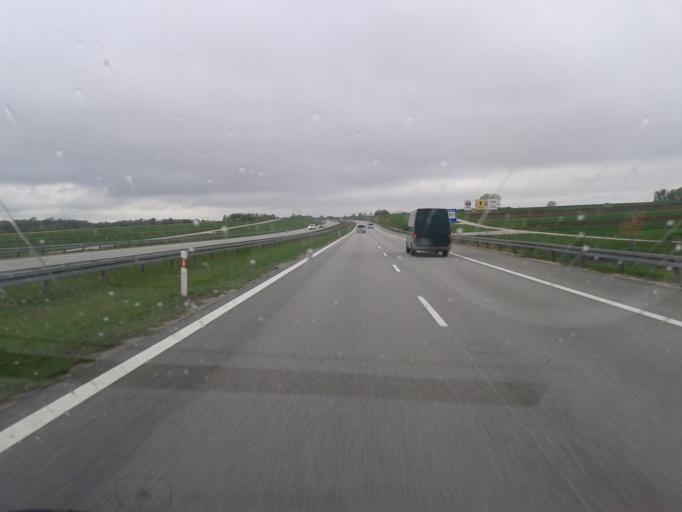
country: PL
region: Subcarpathian Voivodeship
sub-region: Powiat debicki
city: Czarna
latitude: 50.0937
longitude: 21.2956
